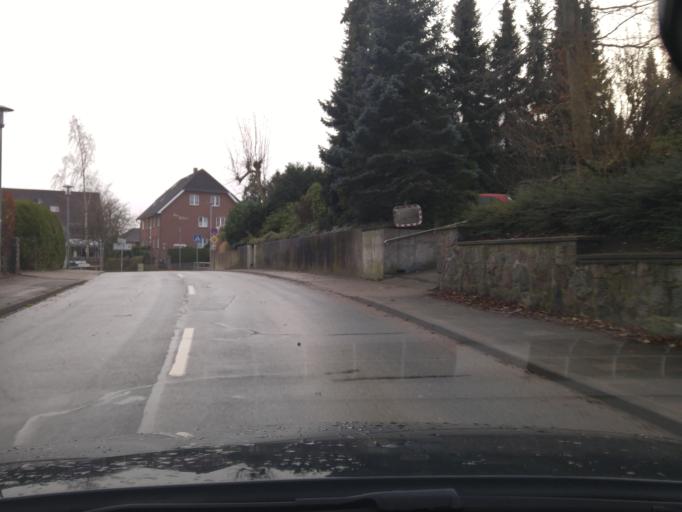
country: DE
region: Schleswig-Holstein
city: Timmendorfer Strand
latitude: 53.9974
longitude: 10.7704
